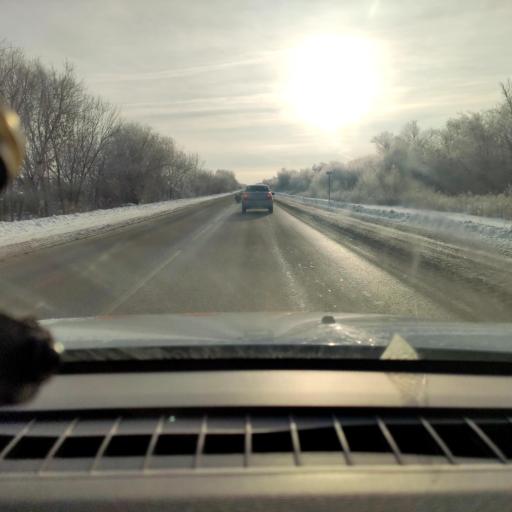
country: RU
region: Samara
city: Samara
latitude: 53.0839
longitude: 50.1601
